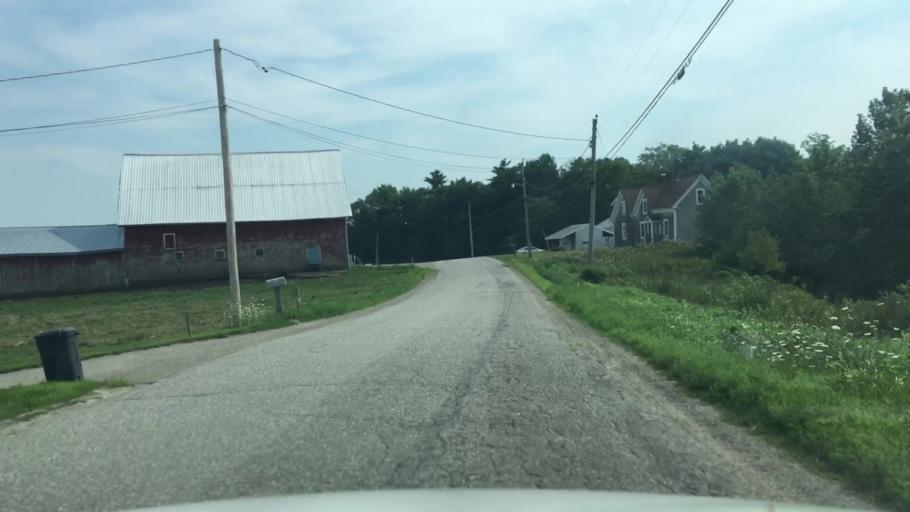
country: US
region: Maine
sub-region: Lincoln County
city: Jefferson
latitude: 44.2187
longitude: -69.4485
